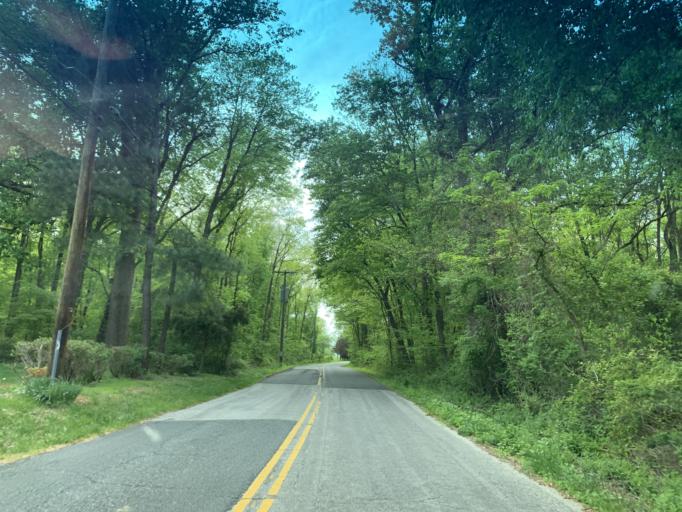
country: US
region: Maryland
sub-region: Harford County
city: South Bel Air
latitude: 39.6432
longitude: -76.2621
